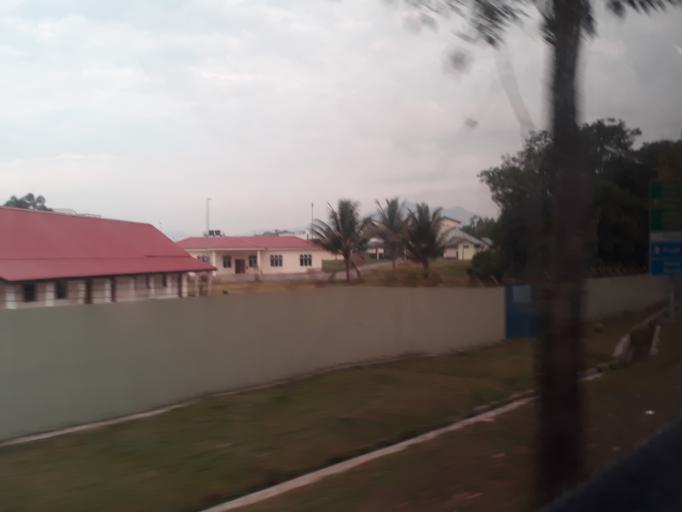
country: MY
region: Perak
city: Ipoh
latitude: 4.6014
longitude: 101.1039
